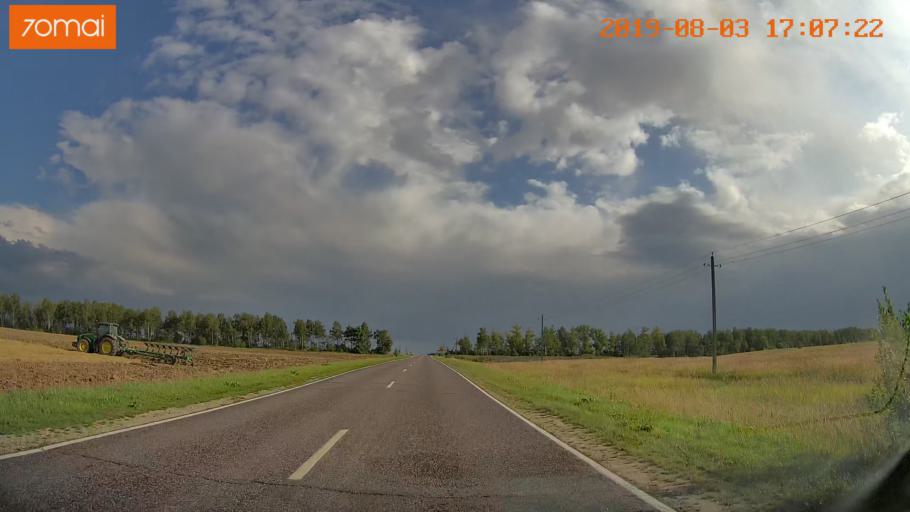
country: RU
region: Moskovskaya
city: Troitskoye
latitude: 55.2966
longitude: 38.5499
